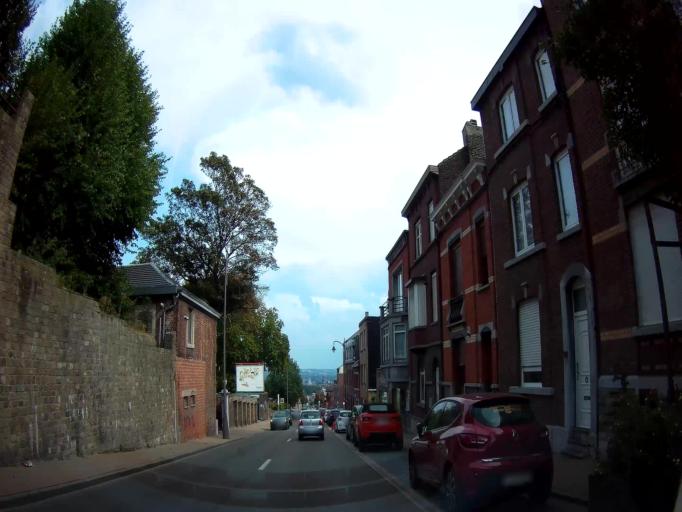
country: BE
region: Wallonia
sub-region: Province de Liege
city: Ans
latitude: 50.6551
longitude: 5.5329
